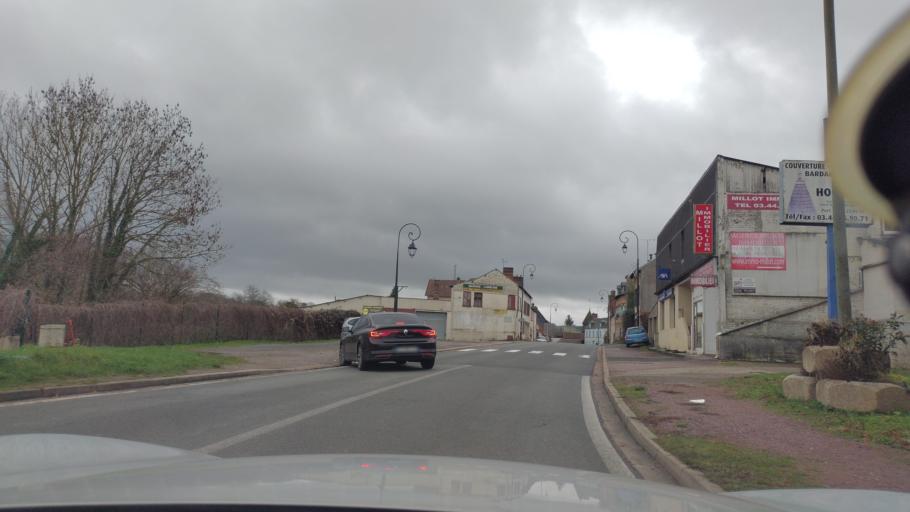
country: FR
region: Picardie
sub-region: Departement de l'Oise
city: Saint-Omer-en-Chaussee
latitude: 49.5788
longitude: 1.9538
